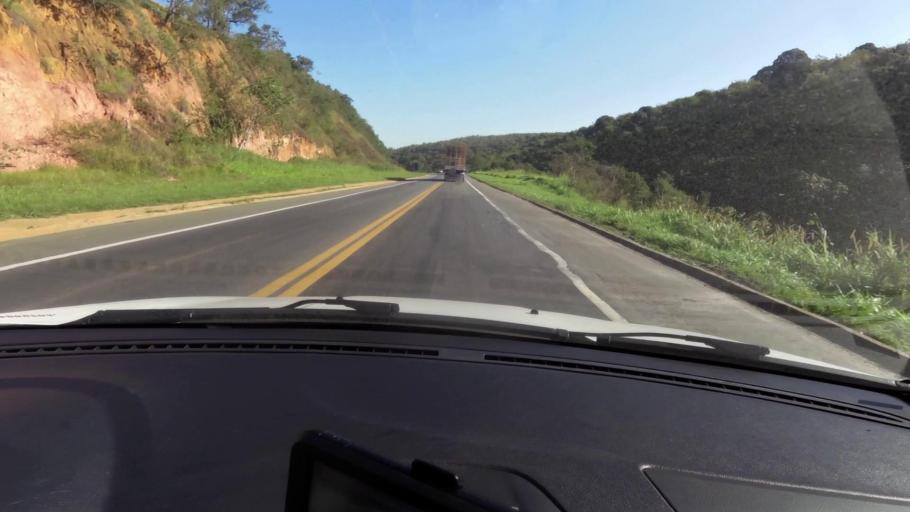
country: BR
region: Espirito Santo
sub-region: Alfredo Chaves
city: Alfredo Chaves
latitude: -20.6766
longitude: -40.6655
